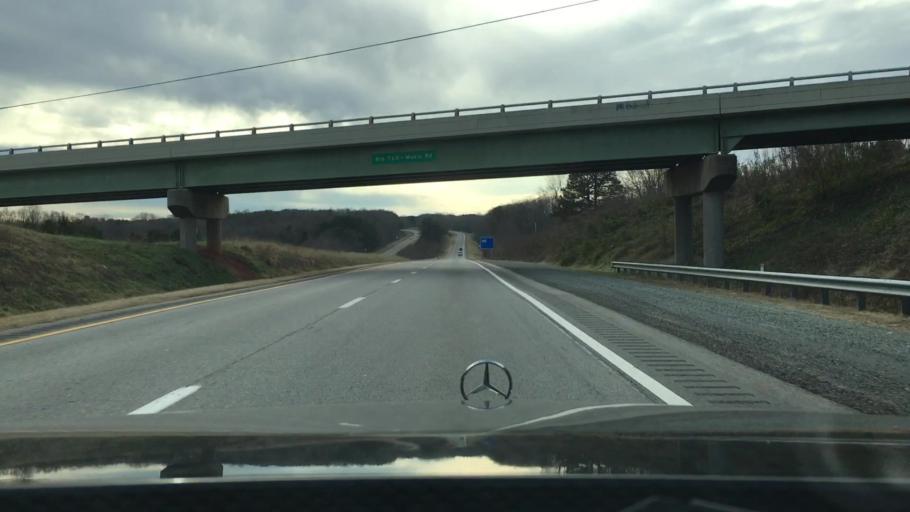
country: US
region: Virginia
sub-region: Pittsylvania County
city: Gretna
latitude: 36.9664
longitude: -79.3672
